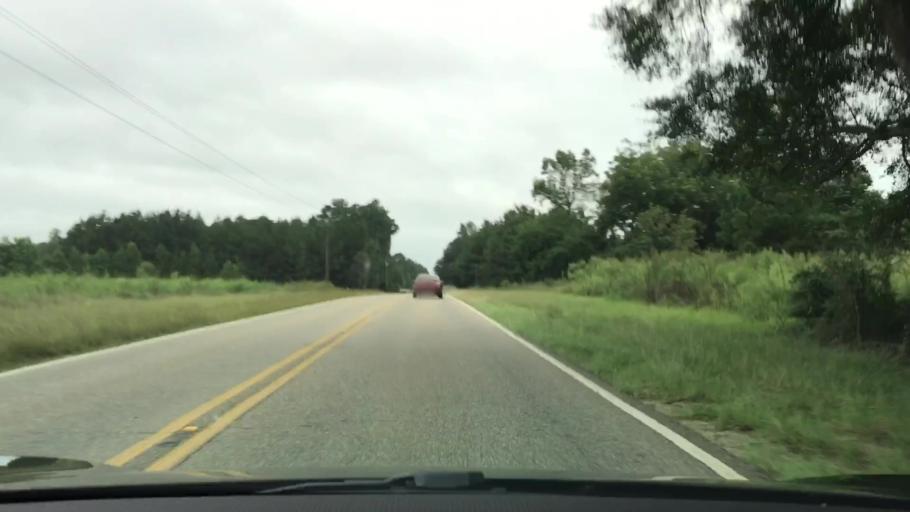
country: US
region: Alabama
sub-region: Geneva County
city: Samson
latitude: 31.1675
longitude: -86.1429
